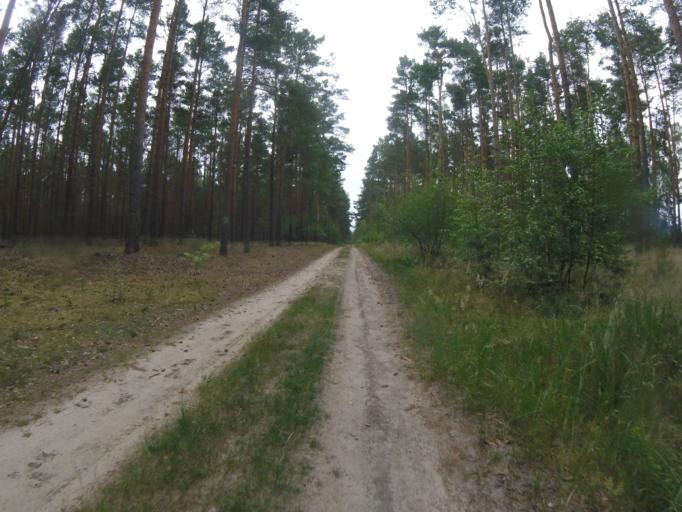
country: DE
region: Brandenburg
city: Gross Koris
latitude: 52.1934
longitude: 13.6616
